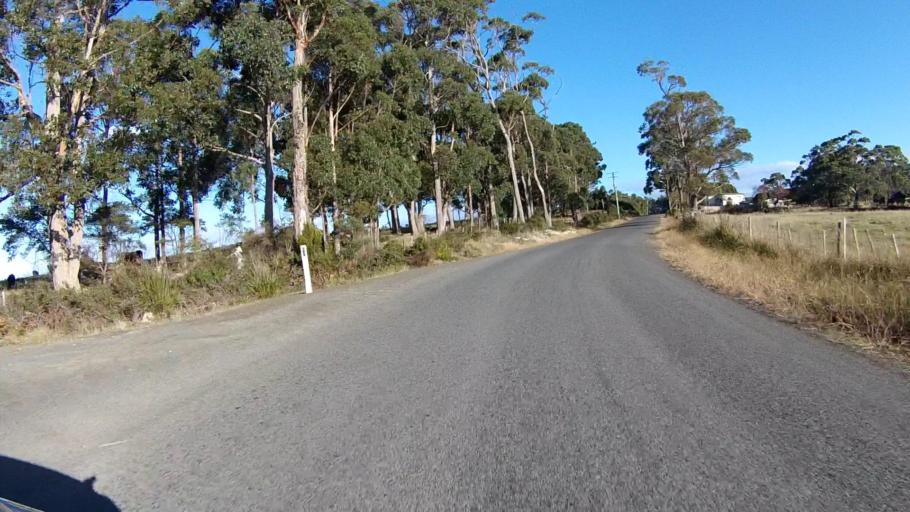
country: AU
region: Tasmania
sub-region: Clarence
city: Sandford
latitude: -43.1669
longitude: 147.8600
